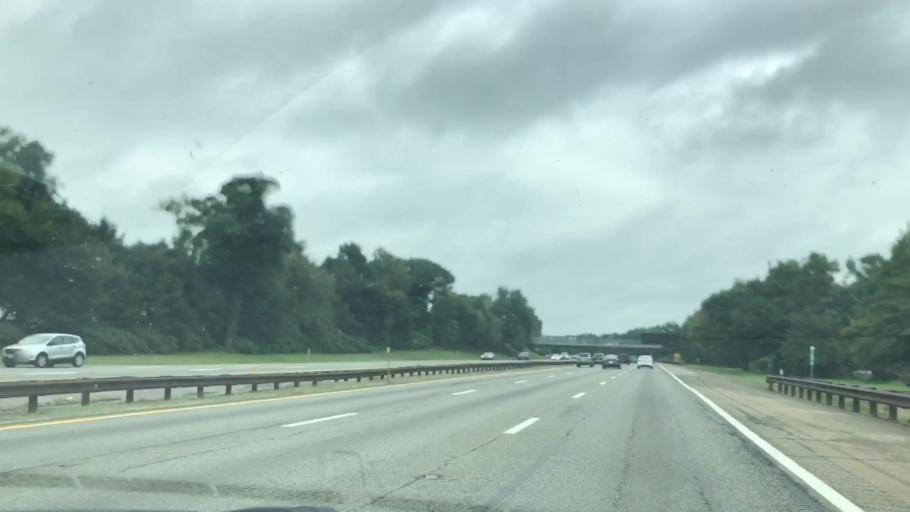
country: US
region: New Jersey
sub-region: Passaic County
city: Clifton
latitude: 40.8662
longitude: -74.1702
